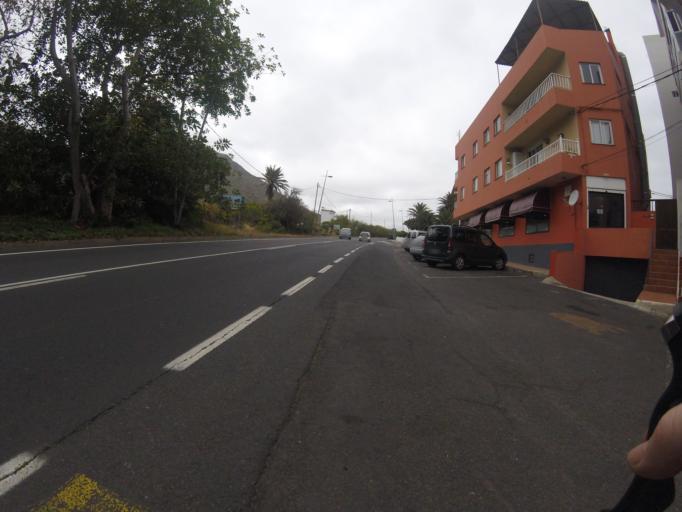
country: ES
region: Canary Islands
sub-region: Provincia de Santa Cruz de Tenerife
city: Tegueste
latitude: 28.5523
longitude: -16.3473
